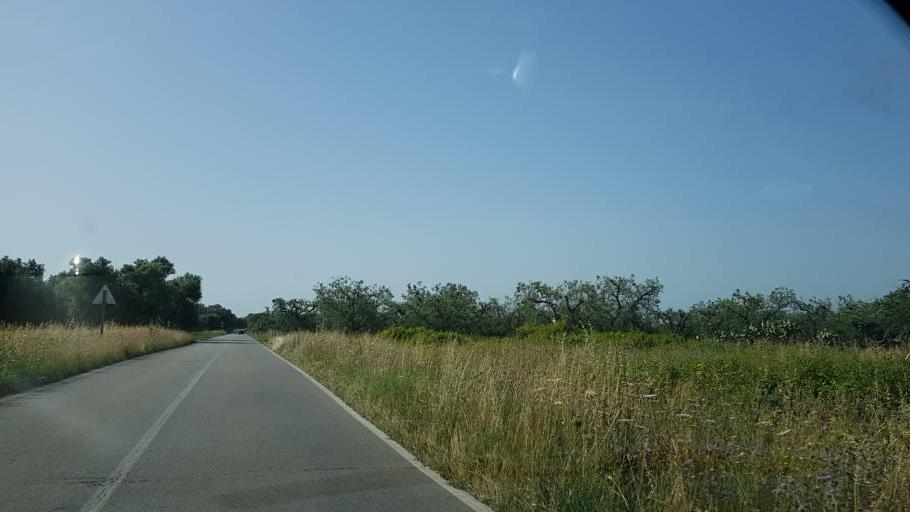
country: IT
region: Apulia
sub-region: Provincia di Brindisi
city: Mesagne
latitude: 40.5207
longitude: 17.8225
